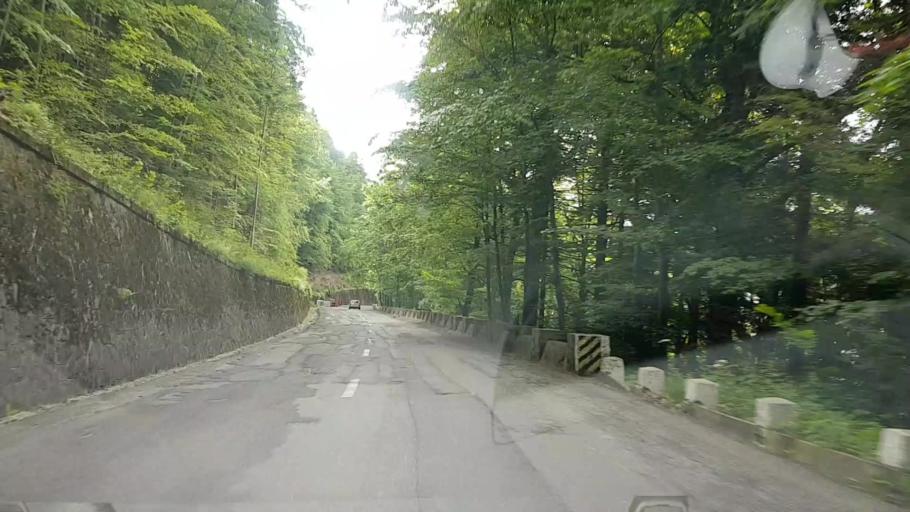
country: RO
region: Neamt
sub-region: Comuna Bicaz
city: Dodeni
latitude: 46.9358
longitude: 26.1202
